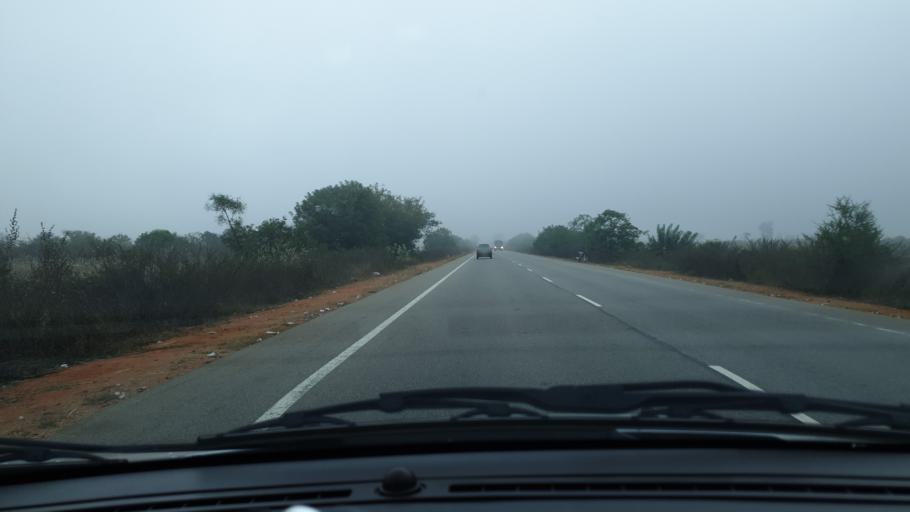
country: IN
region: Telangana
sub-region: Nalgonda
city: Devarkonda
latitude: 16.6307
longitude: 78.6484
